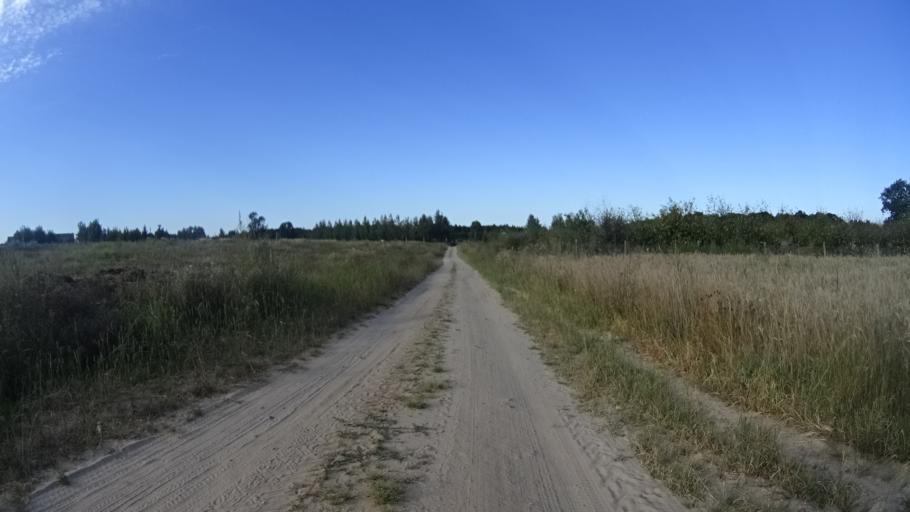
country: PL
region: Masovian Voivodeship
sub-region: Powiat grojecki
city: Goszczyn
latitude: 51.6907
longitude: 20.8148
